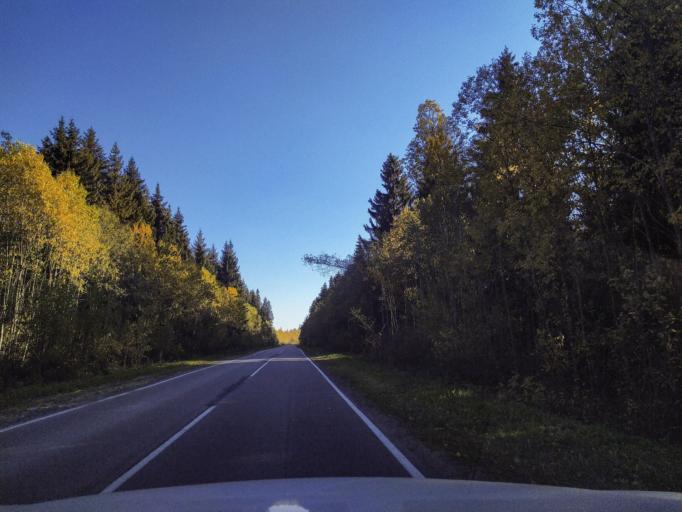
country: RU
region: Leningrad
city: Siverskiy
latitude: 59.3067
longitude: 30.0311
